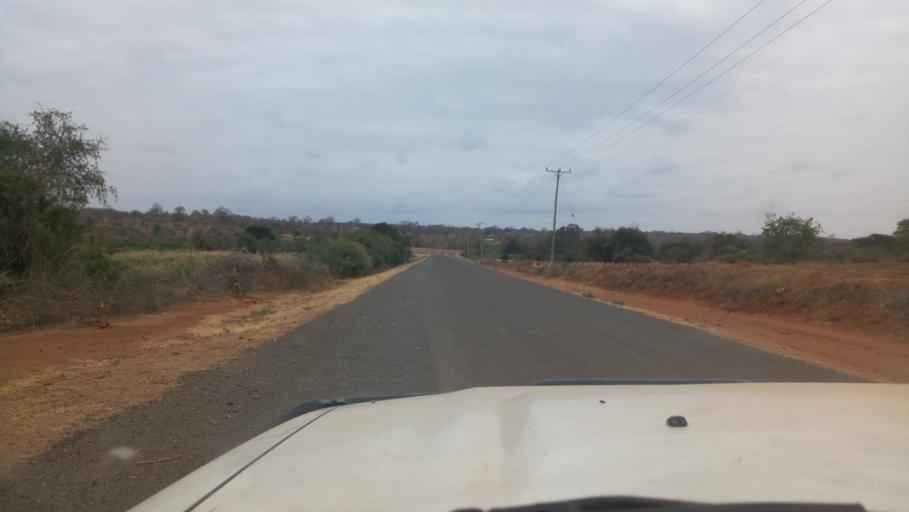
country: KE
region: Makueni
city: Makueni
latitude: -1.9989
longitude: 38.1119
